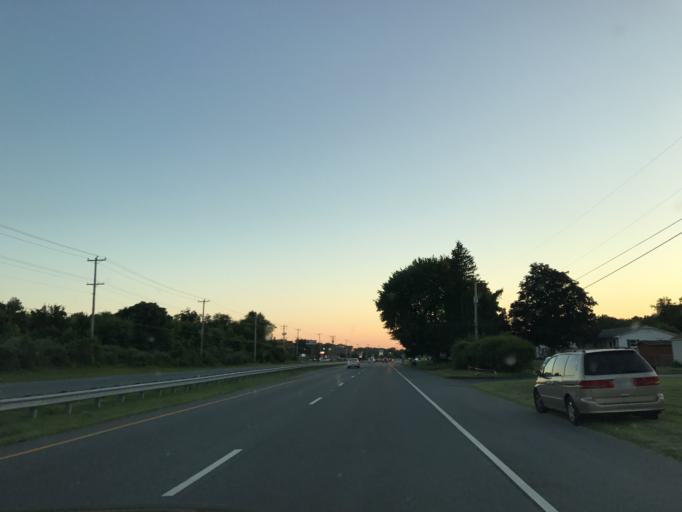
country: US
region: Maryland
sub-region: Cecil County
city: Elkton
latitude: 39.6001
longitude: -75.8077
